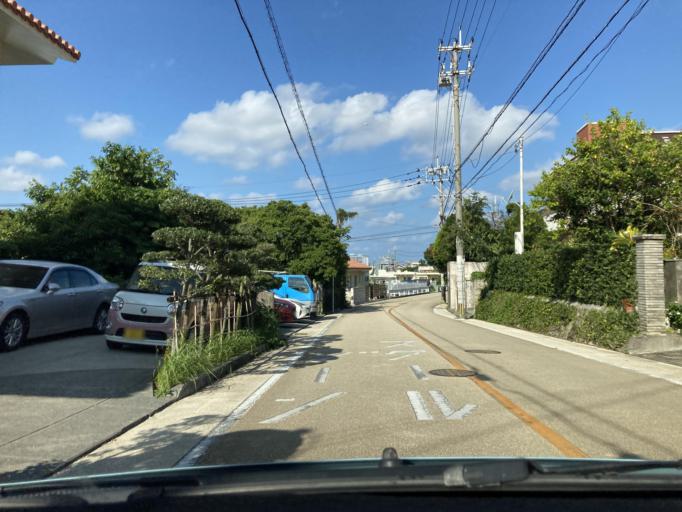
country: JP
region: Okinawa
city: Naha-shi
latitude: 26.2168
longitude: 127.7144
